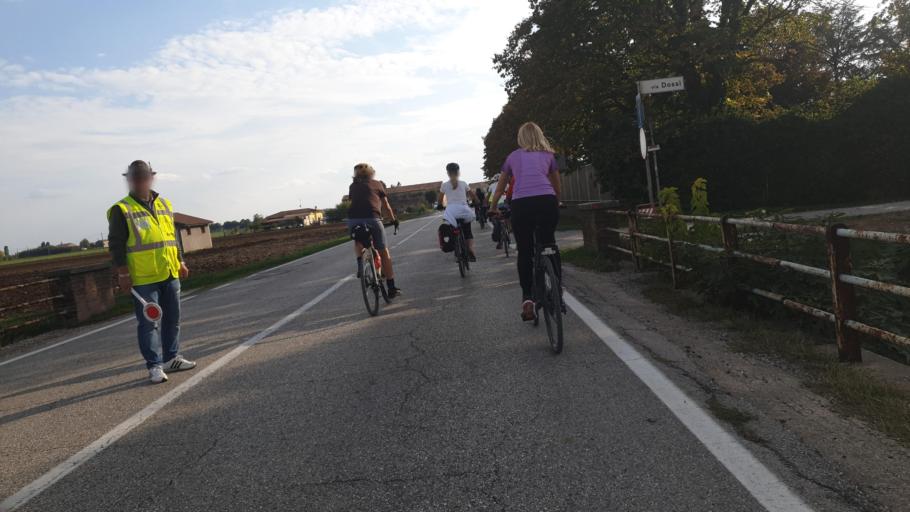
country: IT
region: Veneto
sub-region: Provincia di Vicenza
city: Poiana Maggiore
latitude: 45.2734
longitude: 11.4888
